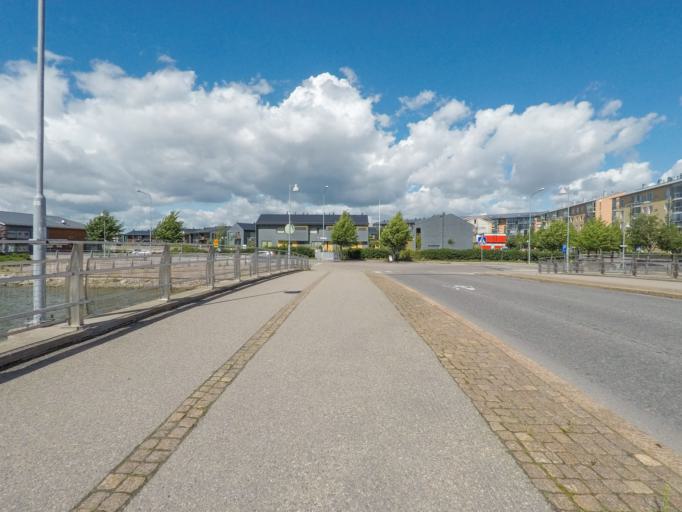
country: FI
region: Uusimaa
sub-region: Helsinki
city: Helsinki
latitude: 60.1872
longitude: 25.0299
